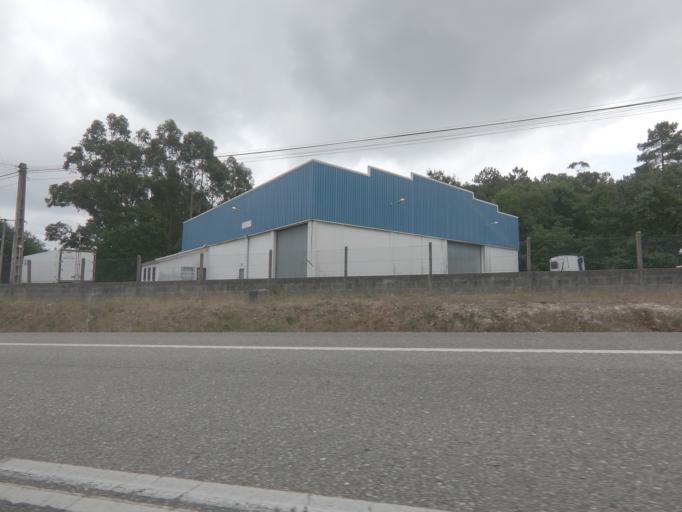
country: PT
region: Viana do Castelo
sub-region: Vila Nova de Cerveira
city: Vila Nova de Cerveira
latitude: 41.9389
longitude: -8.7860
